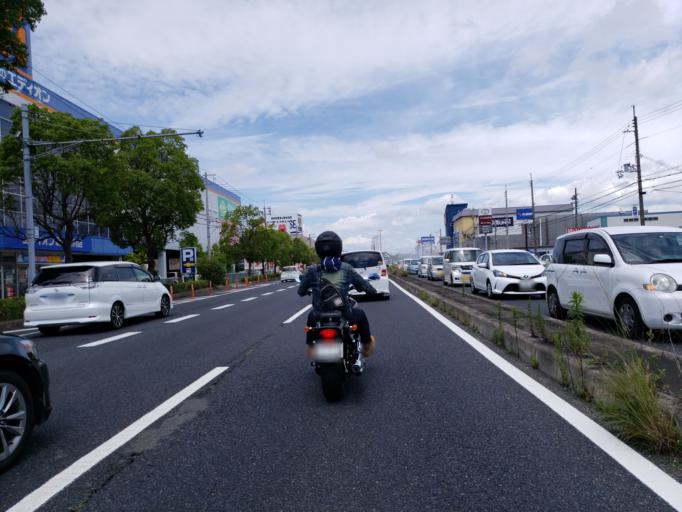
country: JP
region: Hyogo
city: Kakogawacho-honmachi
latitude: 34.7454
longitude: 134.8383
